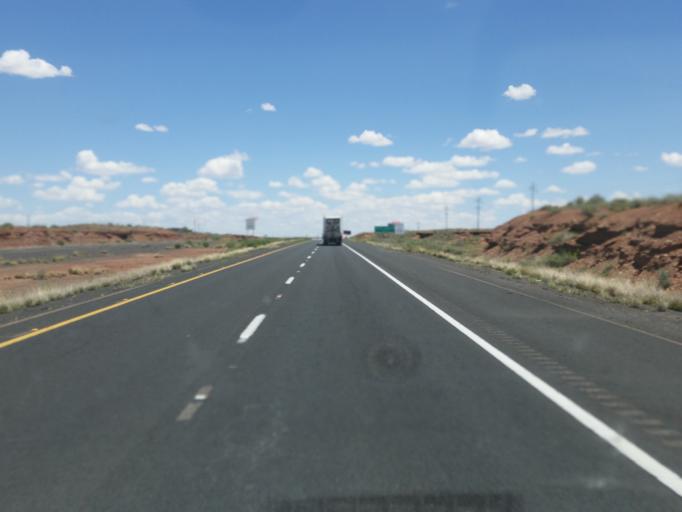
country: US
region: Arizona
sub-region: Navajo County
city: Holbrook
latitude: 34.9093
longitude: -110.2300
